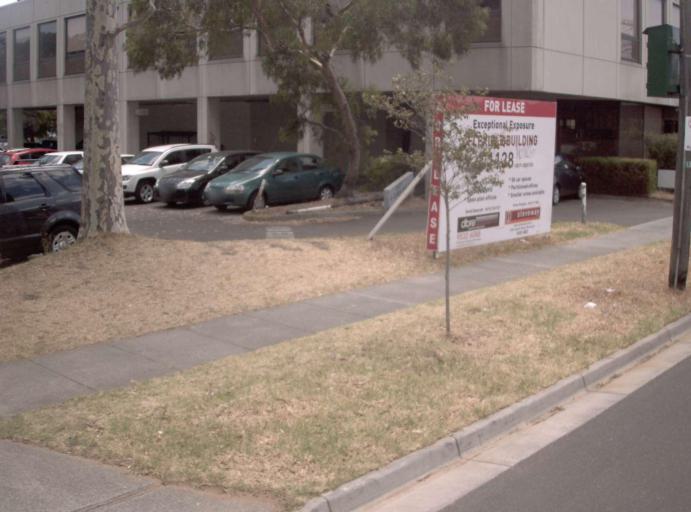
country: AU
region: Victoria
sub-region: Bayside
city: Cheltenham
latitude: -37.9610
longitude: 145.0565
